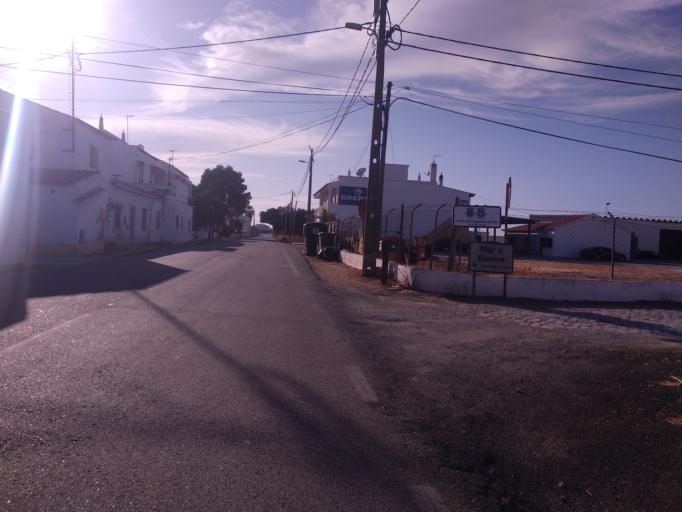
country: PT
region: Faro
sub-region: Faro
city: Faro
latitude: 37.0514
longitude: -7.9324
